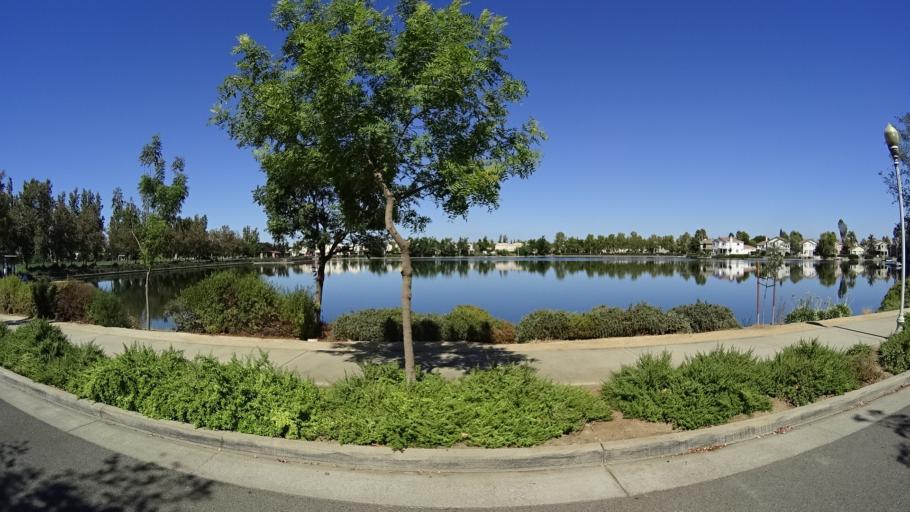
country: US
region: California
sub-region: Sacramento County
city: Laguna
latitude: 38.4204
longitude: -121.4686
